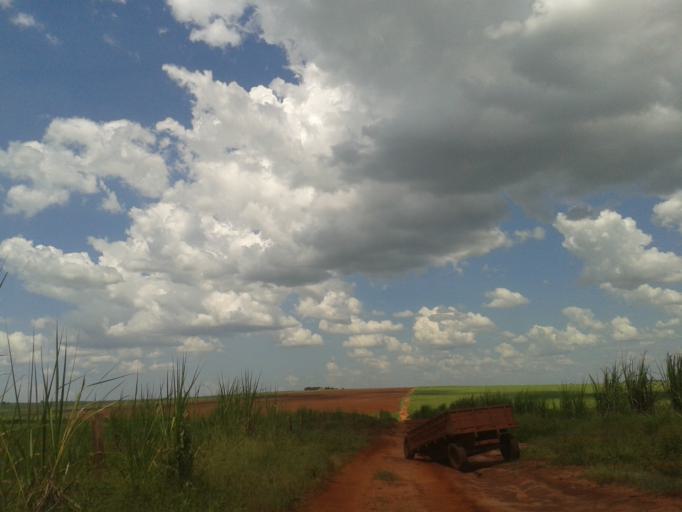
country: BR
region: Minas Gerais
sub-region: Santa Vitoria
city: Santa Vitoria
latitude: -19.1767
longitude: -50.4407
